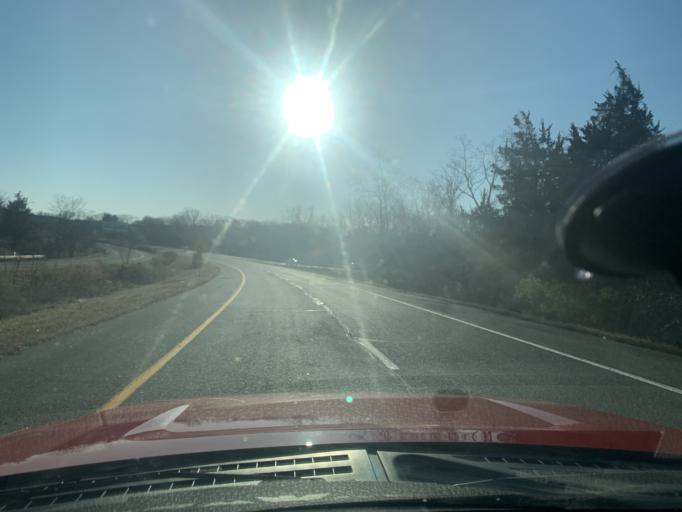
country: US
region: Maryland
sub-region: Anne Arundel County
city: Pumphrey
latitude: 39.2042
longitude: -76.6229
